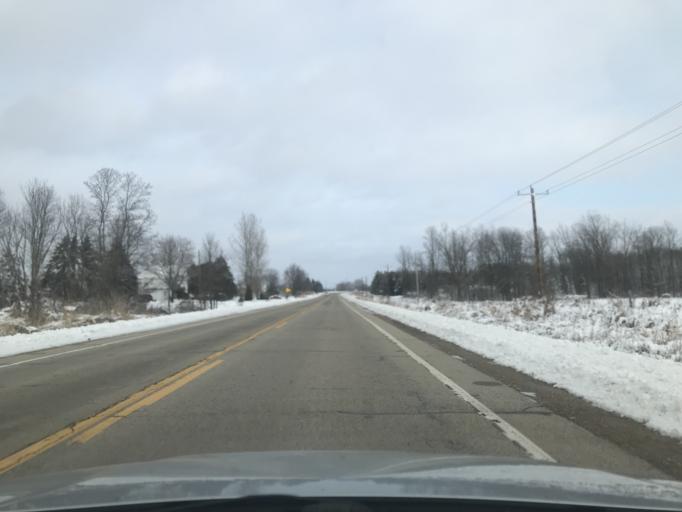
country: US
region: Wisconsin
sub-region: Oconto County
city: Oconto Falls
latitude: 44.8904
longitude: -88.0045
